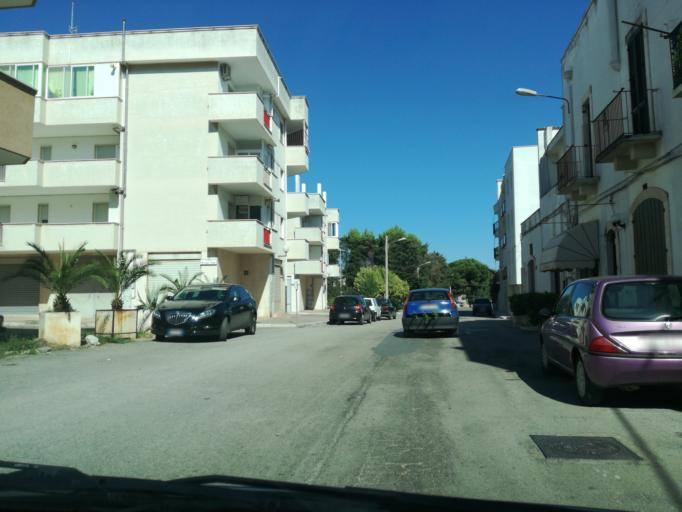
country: IT
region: Apulia
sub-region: Provincia di Bari
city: Castellana
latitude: 40.8898
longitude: 17.1662
